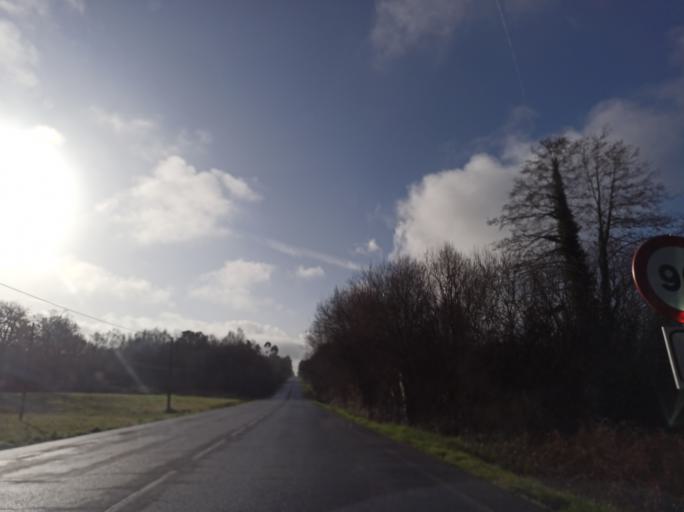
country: ES
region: Galicia
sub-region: Provincia da Coruna
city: Curtis
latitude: 43.1322
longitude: -8.0337
